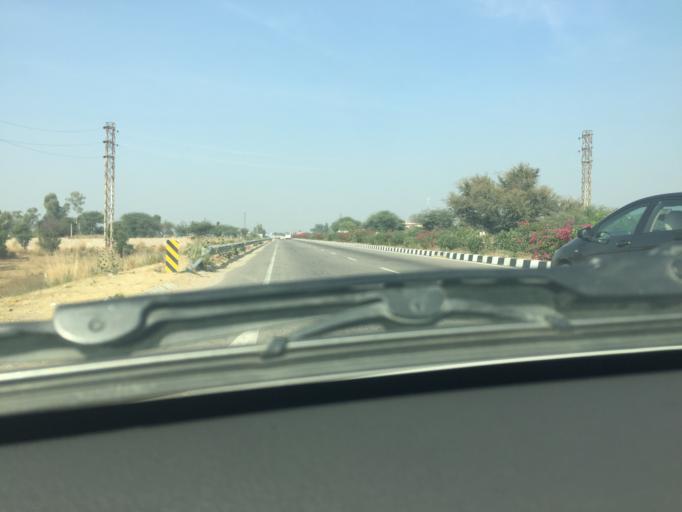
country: IN
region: Rajasthan
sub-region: Sikar
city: Ringas
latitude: 27.3421
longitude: 75.6030
